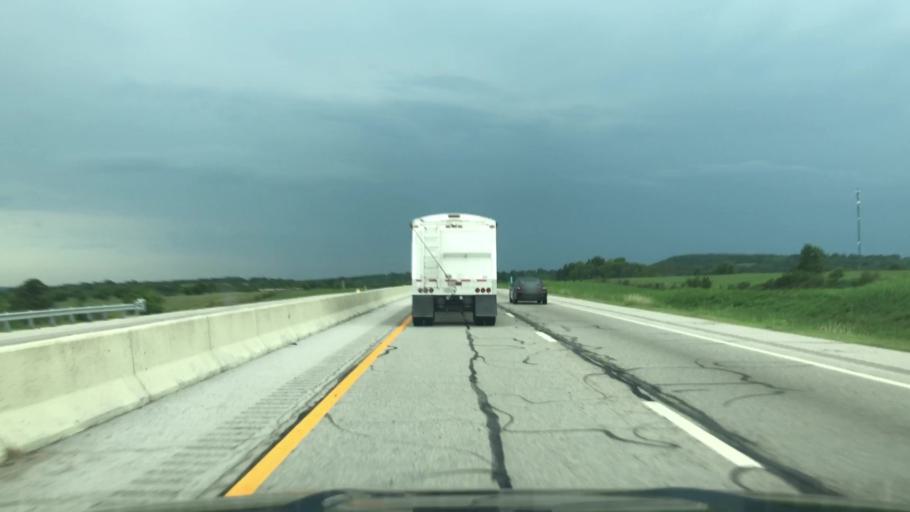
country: US
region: Oklahoma
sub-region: Rogers County
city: Bushyhead
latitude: 36.4084
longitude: -95.4089
